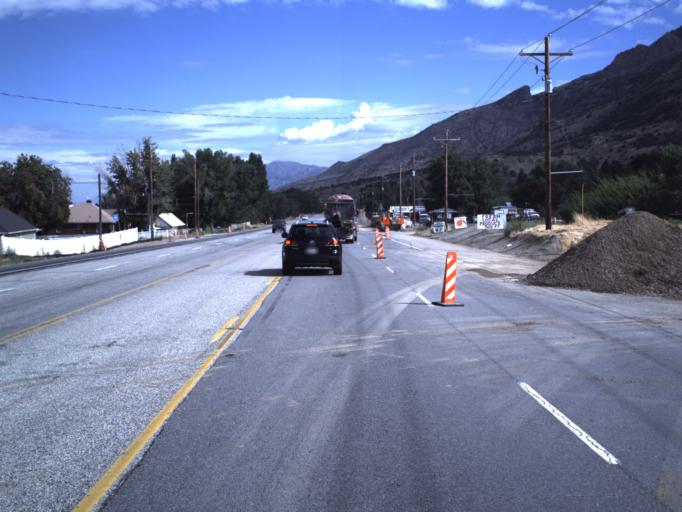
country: US
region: Utah
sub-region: Box Elder County
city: South Willard
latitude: 41.3739
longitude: -112.0334
